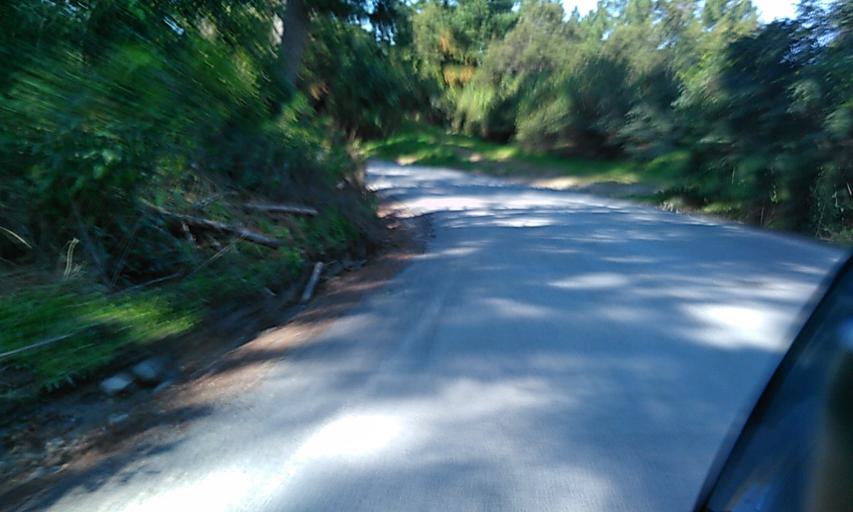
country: NZ
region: Gisborne
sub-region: Gisborne District
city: Gisborne
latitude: -38.3169
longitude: 178.1335
